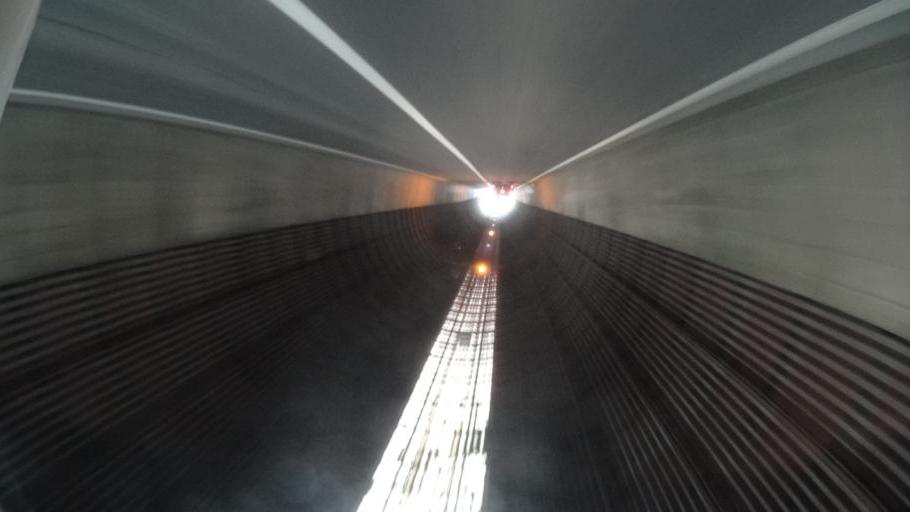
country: JP
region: Fukui
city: Ono
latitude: 35.9659
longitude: 136.5975
